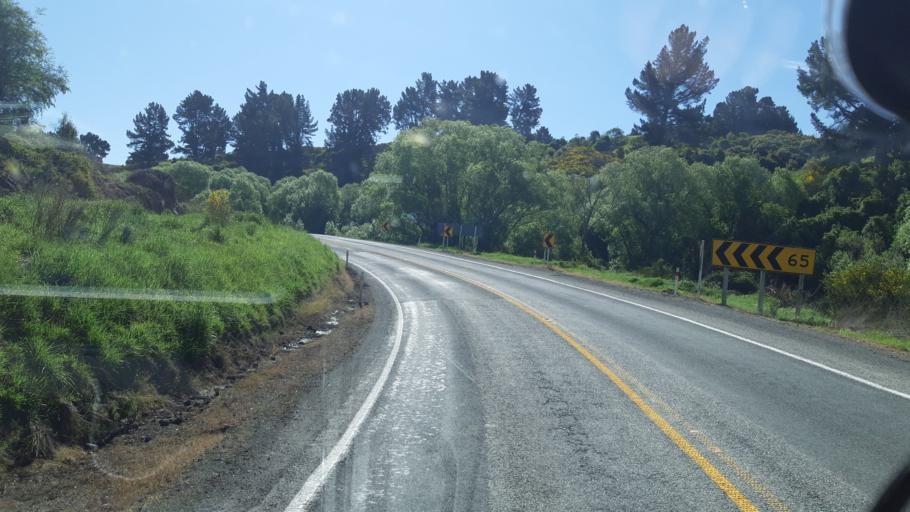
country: NZ
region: Otago
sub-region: Clutha District
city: Milton
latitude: -46.0617
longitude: 169.8202
